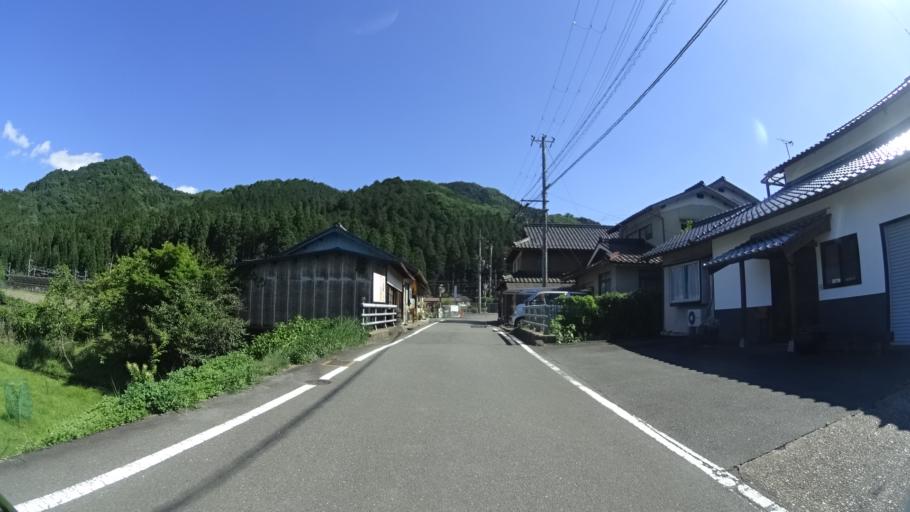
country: JP
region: Kyoto
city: Fukuchiyama
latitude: 35.3303
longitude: 135.0731
